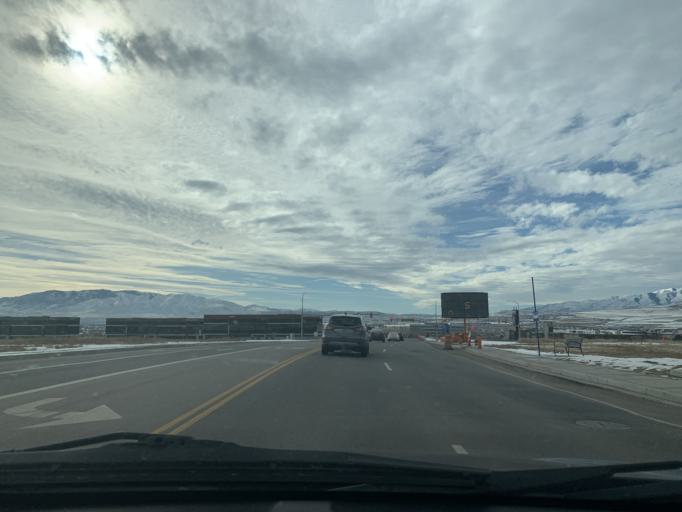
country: US
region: Utah
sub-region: Utah County
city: Lehi
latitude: 40.4256
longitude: -111.8807
